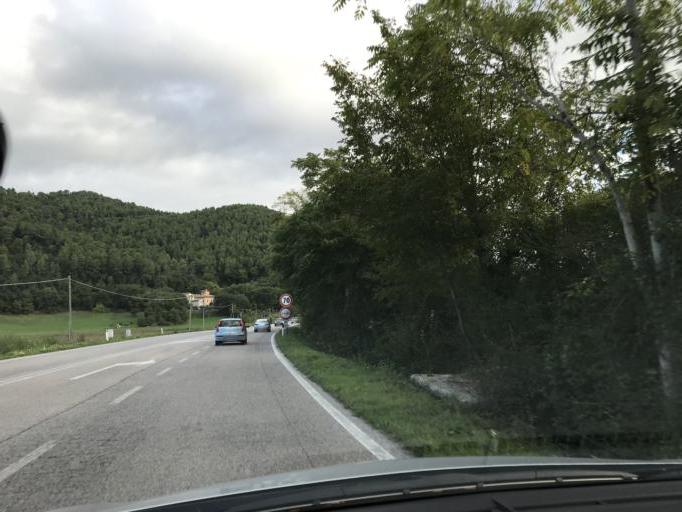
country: IT
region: Umbria
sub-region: Provincia di Perugia
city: Spoleto
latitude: 42.7087
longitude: 12.7192
